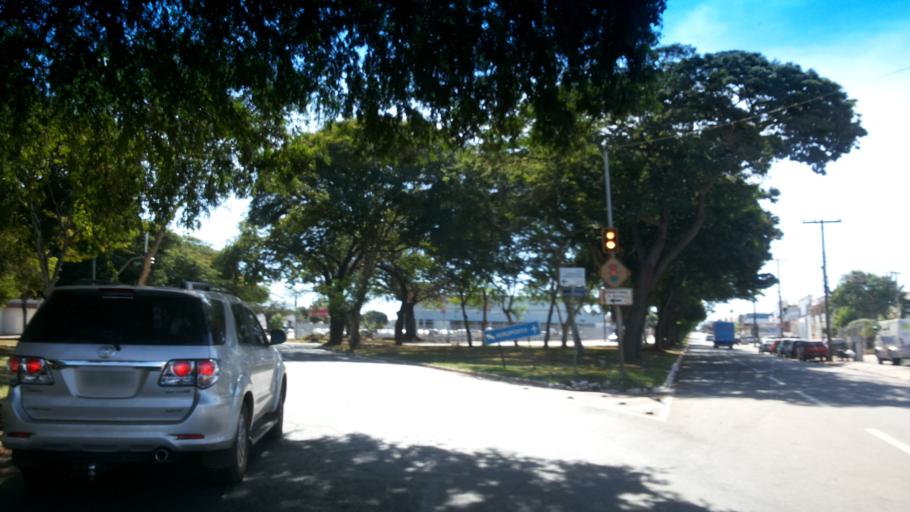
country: BR
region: Goias
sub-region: Goiania
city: Goiania
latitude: -16.6400
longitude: -49.2398
